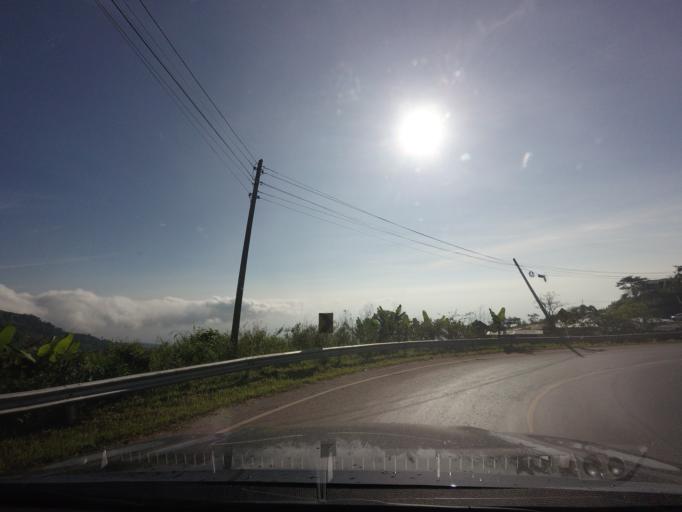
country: TH
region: Phetchabun
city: Lom Kao
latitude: 16.8825
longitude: 101.1013
